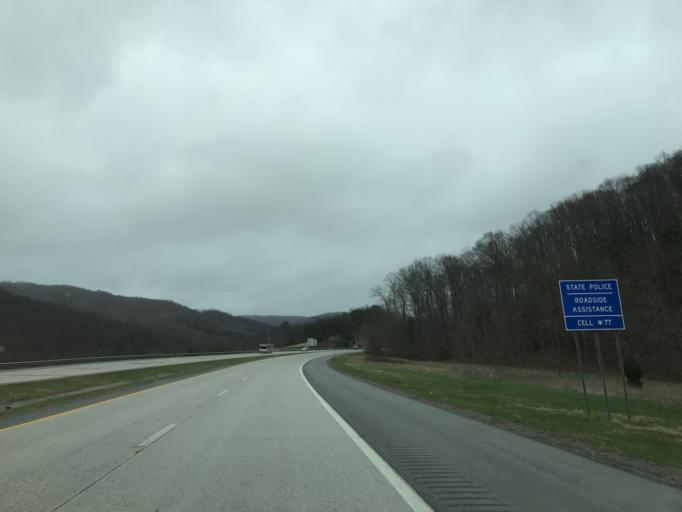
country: US
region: West Virginia
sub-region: Summers County
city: Hinton
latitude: 37.7899
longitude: -80.8749
